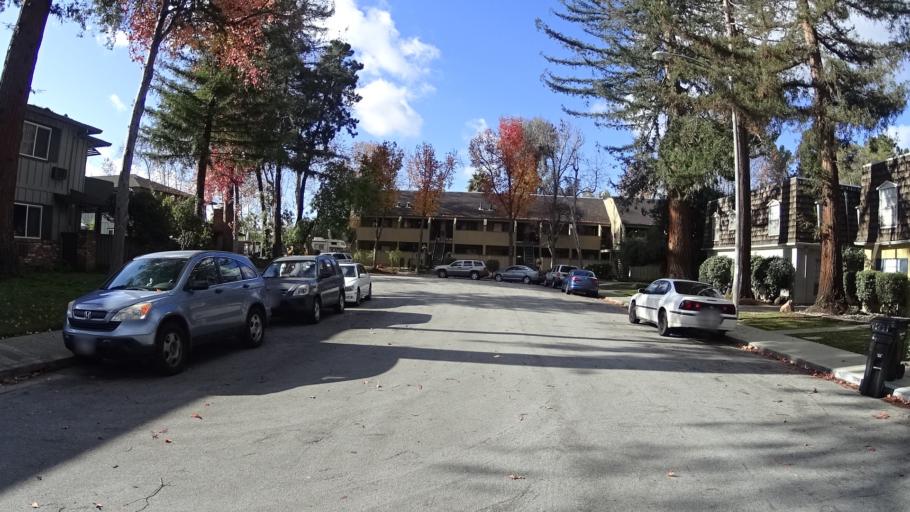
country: US
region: California
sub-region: Santa Clara County
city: Sunnyvale
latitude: 37.3837
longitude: -122.0554
